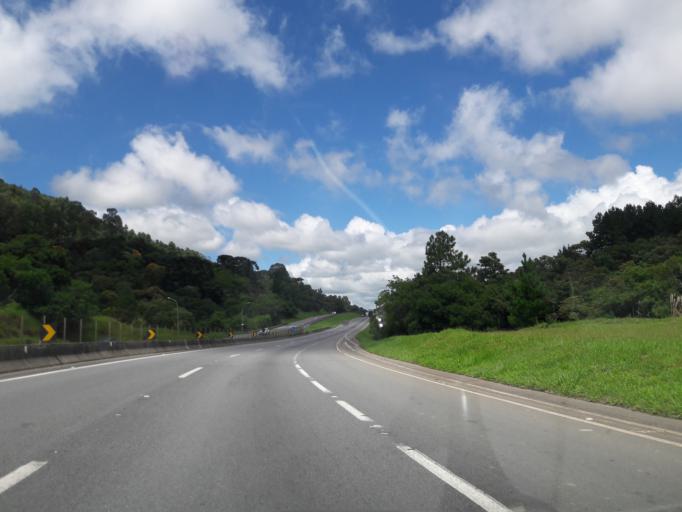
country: BR
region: Parana
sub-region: Campina Grande Do Sul
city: Campina Grande do Sul
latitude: -25.1405
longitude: -48.8561
